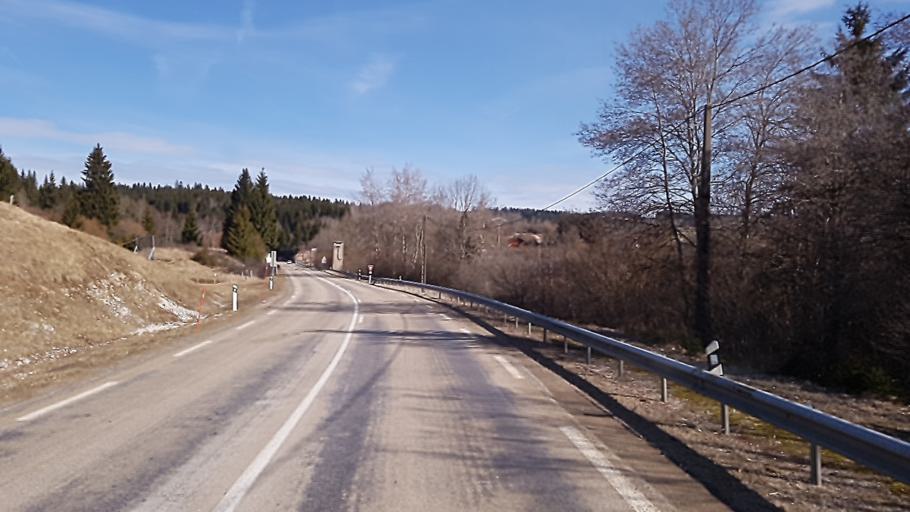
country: FR
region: Franche-Comte
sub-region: Departement du Jura
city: Morbier
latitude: 46.6183
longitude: 5.9597
